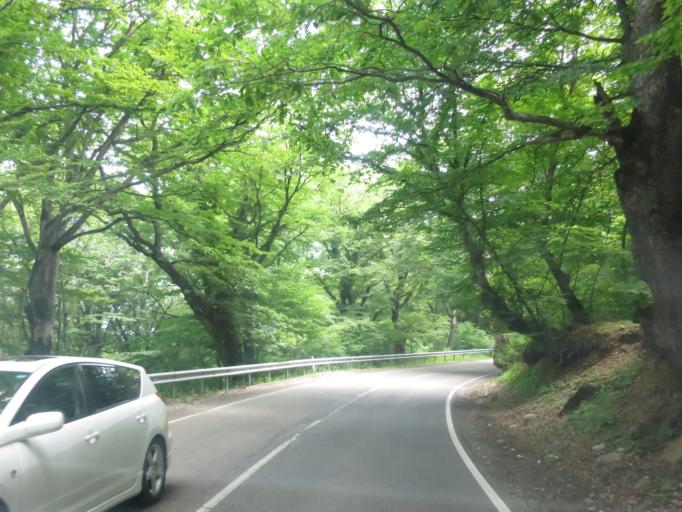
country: GE
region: Kakheti
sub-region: Telavi
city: Telavi
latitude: 41.9222
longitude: 45.3956
